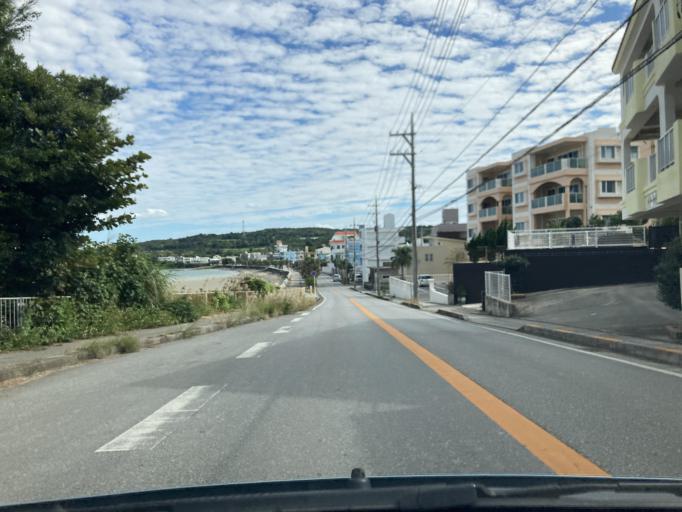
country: JP
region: Okinawa
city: Ishikawa
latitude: 26.4224
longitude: 127.7355
